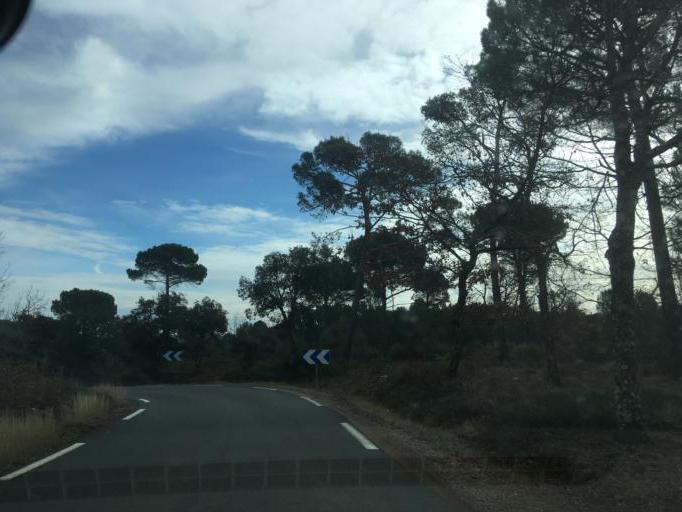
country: FR
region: Provence-Alpes-Cote d'Azur
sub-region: Departement du Var
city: Bras
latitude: 43.4473
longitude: 5.9924
